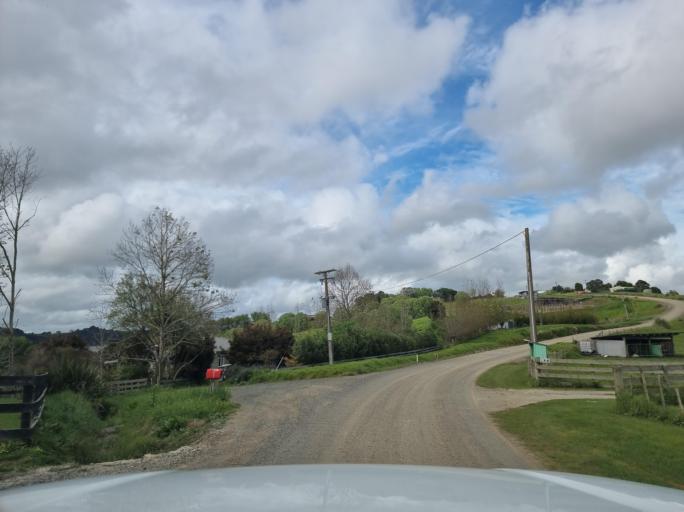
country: NZ
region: Northland
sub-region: Whangarei
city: Ruakaka
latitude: -36.1213
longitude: 174.2102
